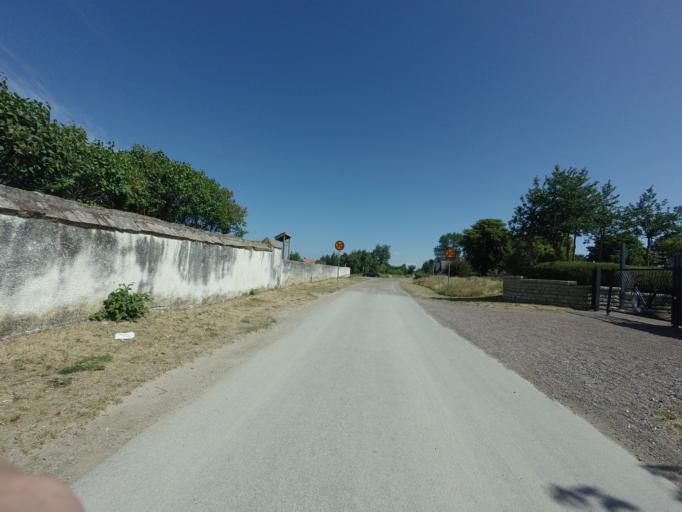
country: SE
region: Skane
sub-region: Vellinge Kommun
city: Skanor med Falsterbo
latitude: 55.4197
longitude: 12.8503
